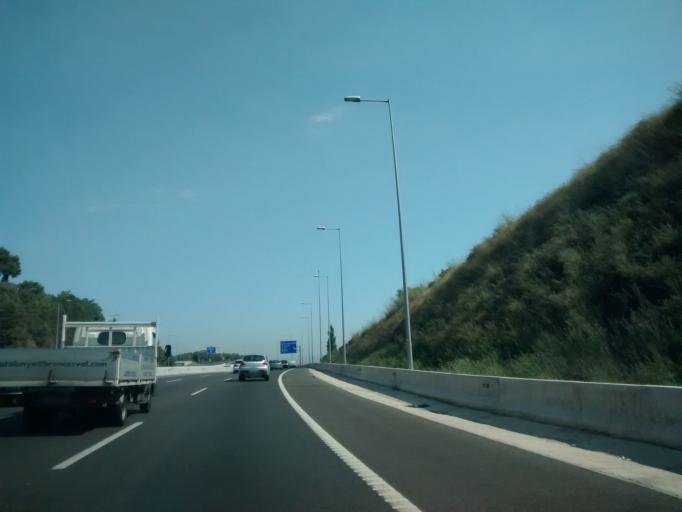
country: ES
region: Catalonia
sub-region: Provincia de Barcelona
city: Montcada i Reixac
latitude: 41.4740
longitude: 2.1632
